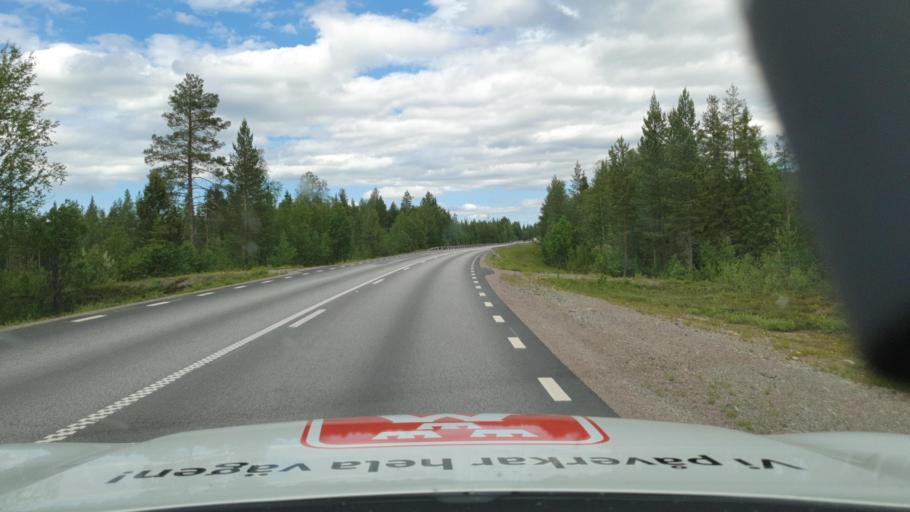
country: SE
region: Vaesterbotten
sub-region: Norsjo Kommun
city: Norsjoe
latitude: 65.1461
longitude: 19.8960
